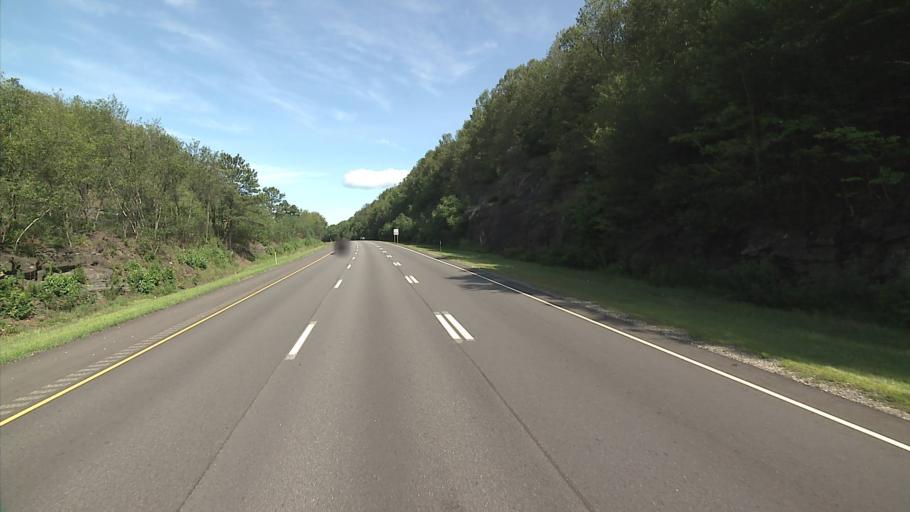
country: US
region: Connecticut
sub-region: Hartford County
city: Terramuggus
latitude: 41.6415
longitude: -72.4632
